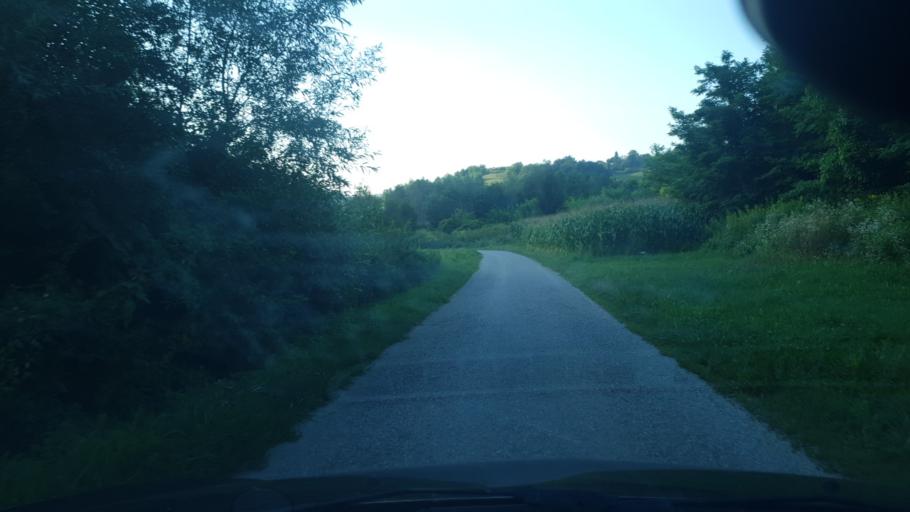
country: HR
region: Krapinsko-Zagorska
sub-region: Grad Krapina
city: Krapina
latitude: 46.1432
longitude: 15.8585
